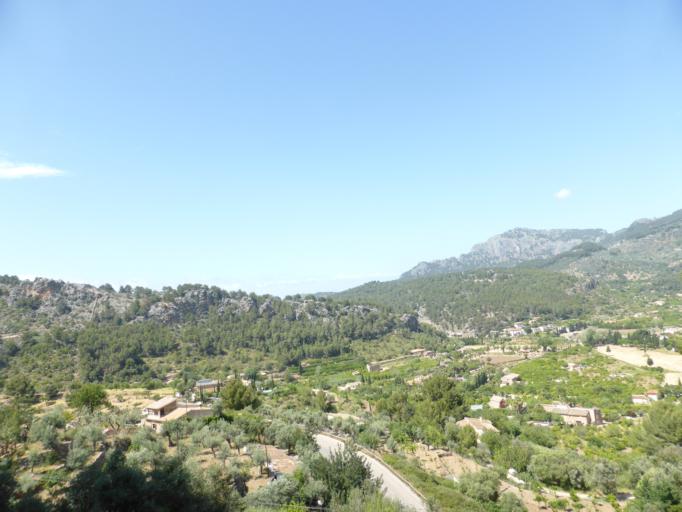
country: ES
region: Balearic Islands
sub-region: Illes Balears
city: Soller
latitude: 39.7738
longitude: 2.6970
